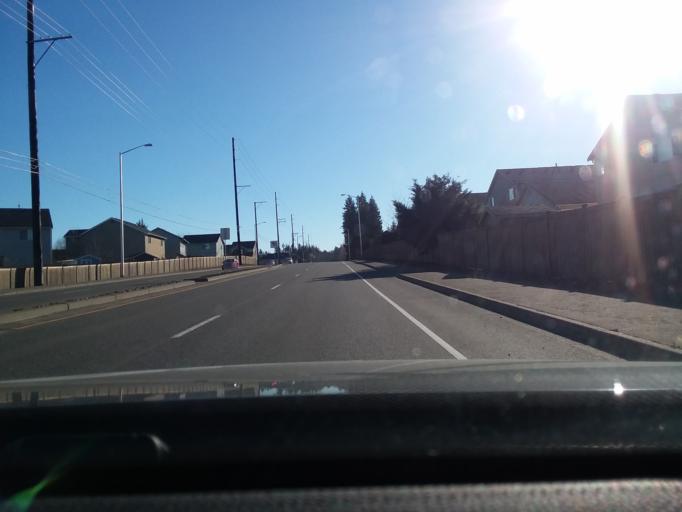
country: US
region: Washington
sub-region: Pierce County
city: Graham
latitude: 47.0963
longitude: -122.3113
